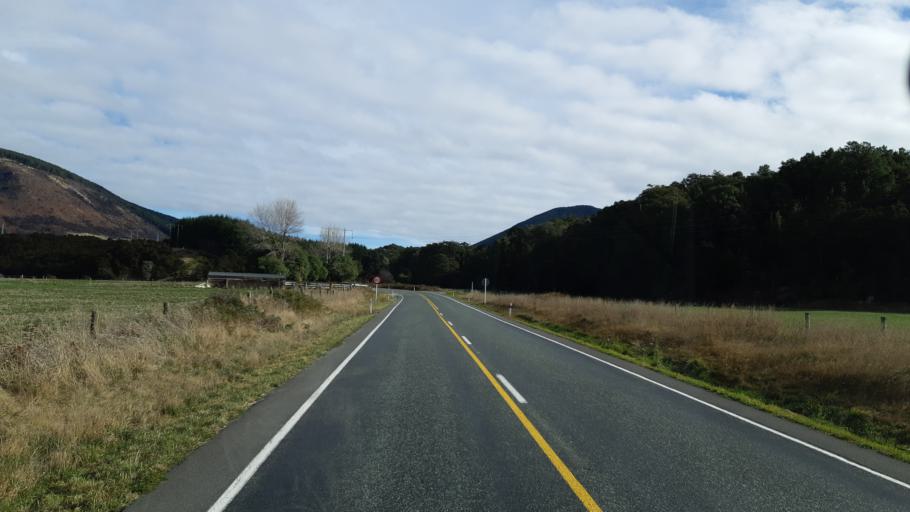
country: NZ
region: Tasman
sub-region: Tasman District
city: Wakefield
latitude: -41.7676
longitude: 172.9642
